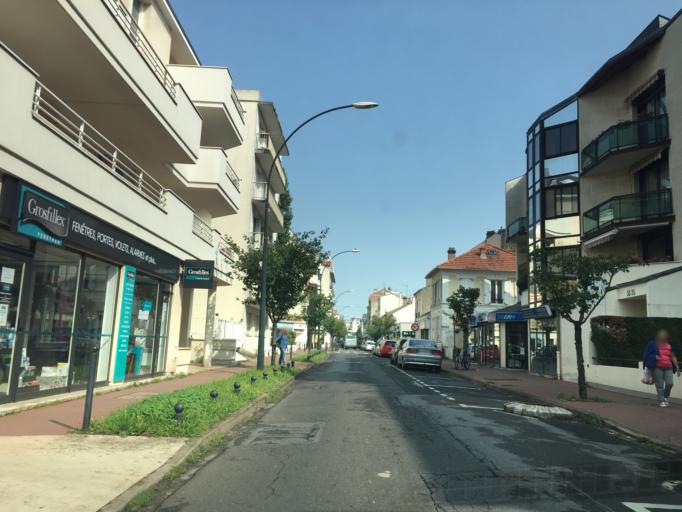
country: FR
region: Ile-de-France
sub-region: Departement du Val-de-Marne
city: Saint-Maur-des-Fosses
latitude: 48.8009
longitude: 2.4860
